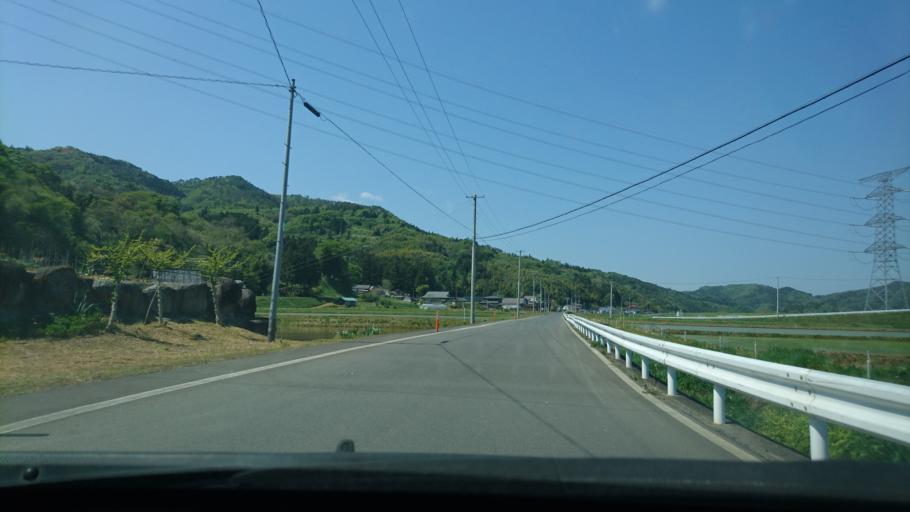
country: JP
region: Iwate
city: Ichinoseki
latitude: 38.9327
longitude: 141.2457
